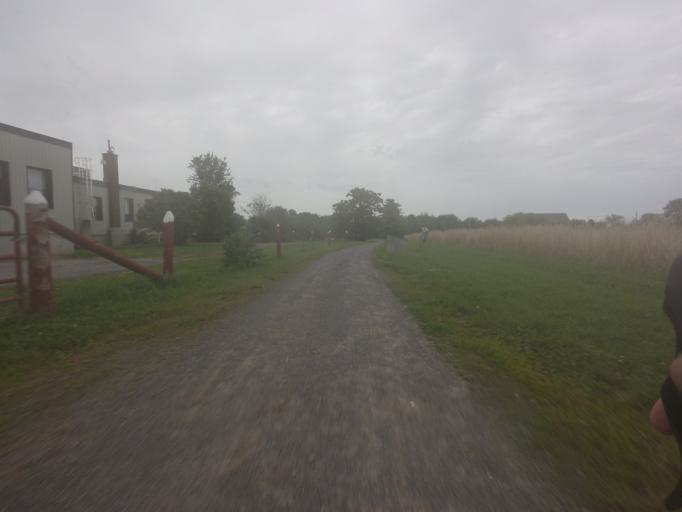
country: CA
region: Ontario
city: Ottawa
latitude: 45.3853
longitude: -75.7089
